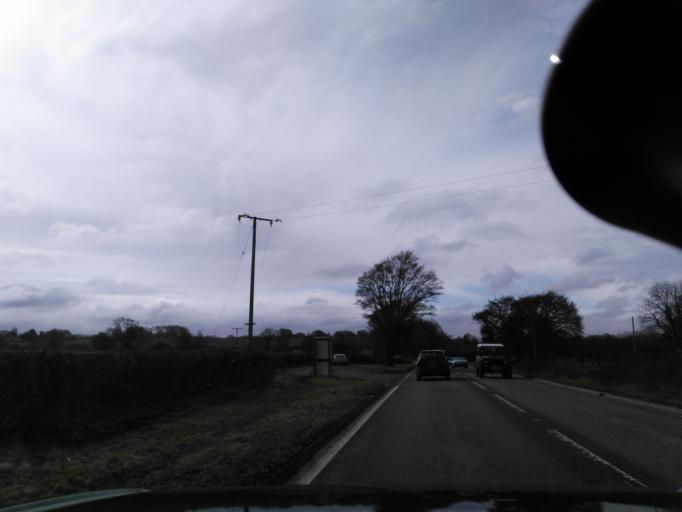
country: GB
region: England
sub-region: Wiltshire
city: Trowbridge
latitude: 51.3141
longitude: -2.1682
